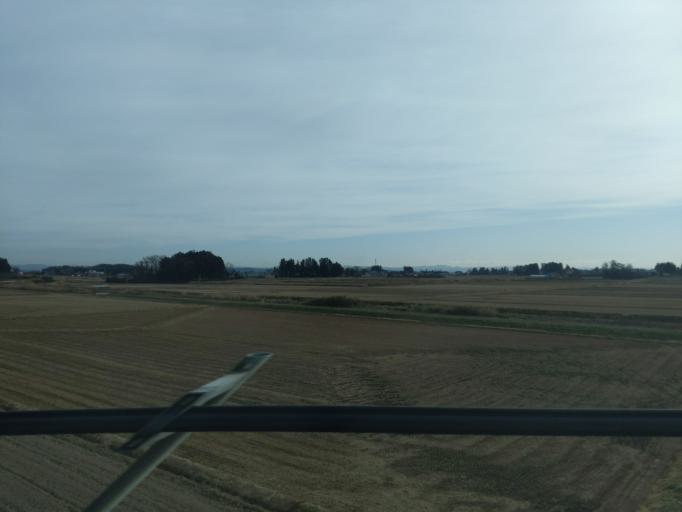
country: JP
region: Iwate
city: Ichinoseki
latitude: 38.7761
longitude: 141.0872
